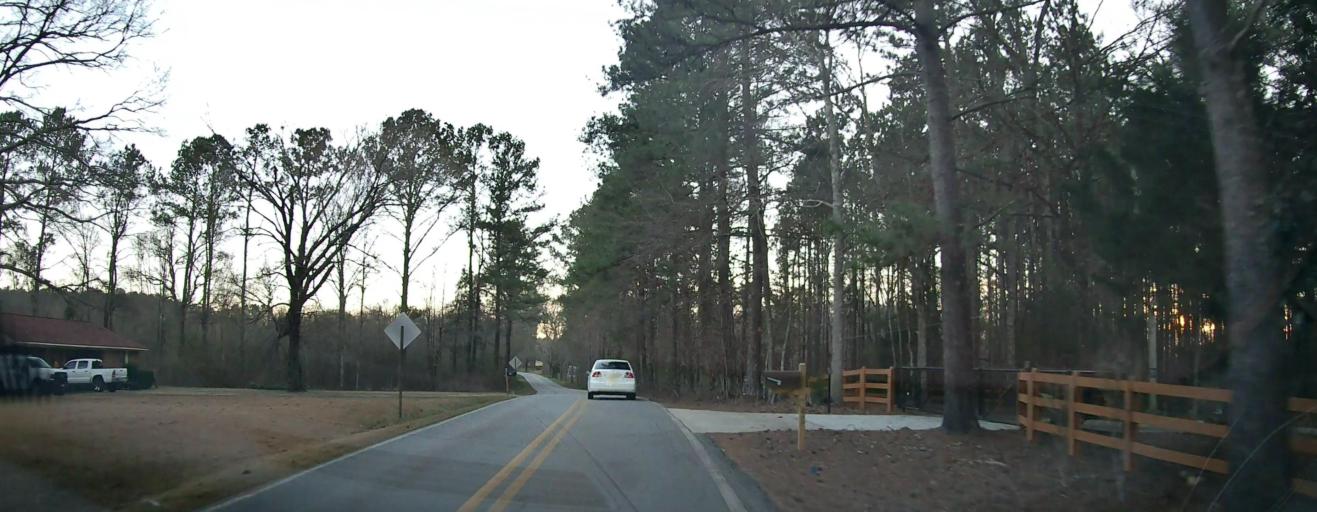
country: US
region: Georgia
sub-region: Troup County
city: La Grange
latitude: 33.0607
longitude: -84.9682
